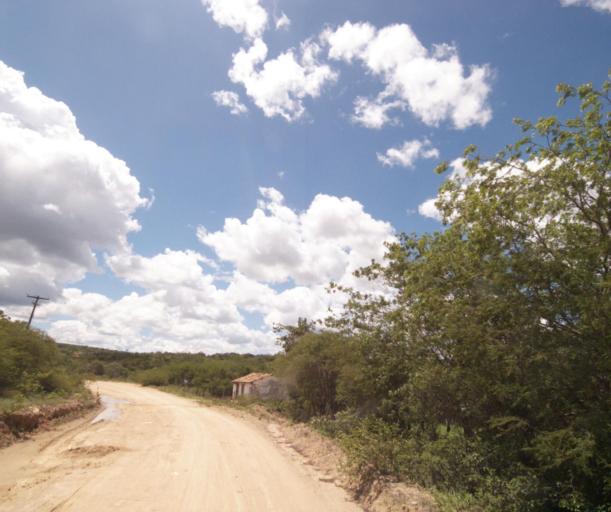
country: BR
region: Bahia
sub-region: Pocoes
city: Pocoes
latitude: -14.3804
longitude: -40.5596
